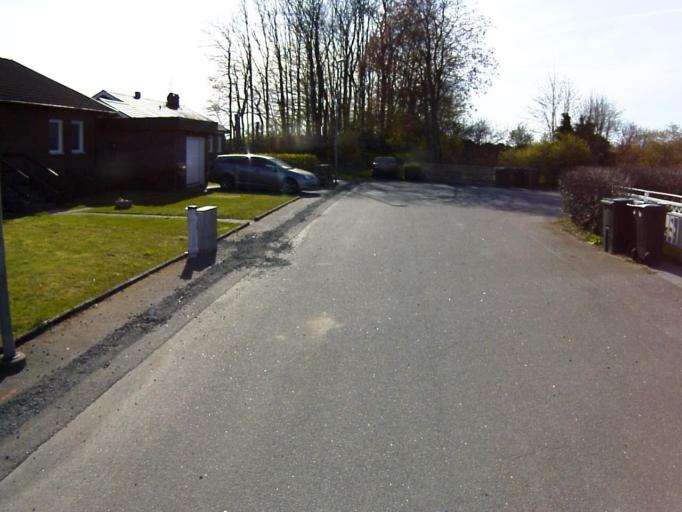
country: SE
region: Skane
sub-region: Kristianstads Kommun
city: Onnestad
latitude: 55.9948
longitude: 14.0319
